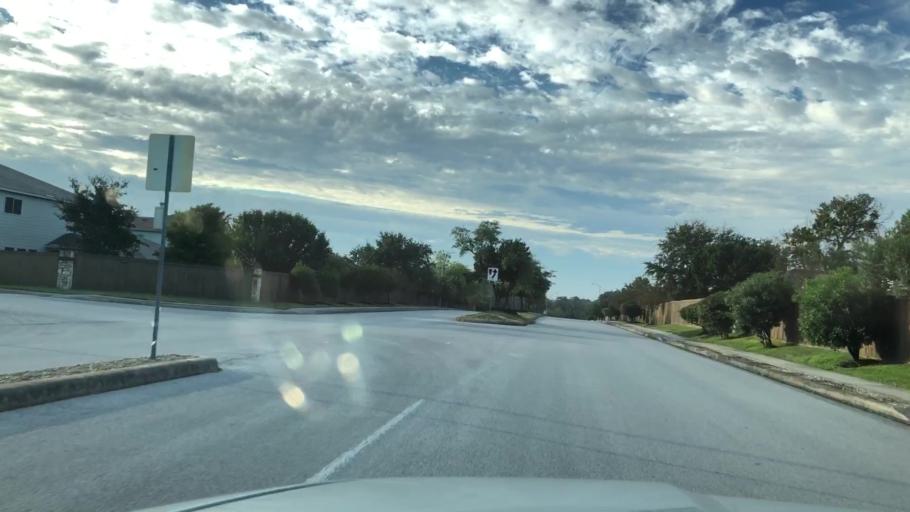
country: US
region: Texas
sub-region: Bexar County
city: Helotes
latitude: 29.5480
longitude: -98.6465
